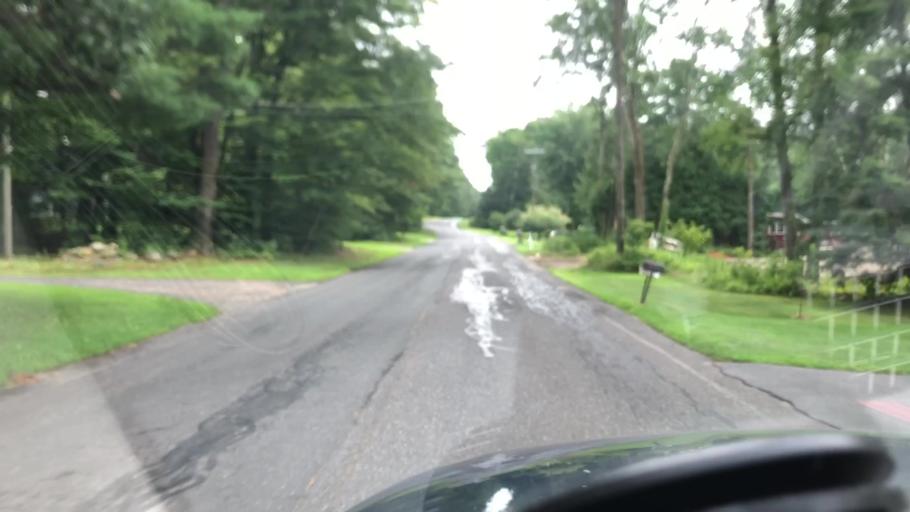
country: US
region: Massachusetts
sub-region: Hampshire County
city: Easthampton
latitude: 42.2475
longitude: -72.6951
